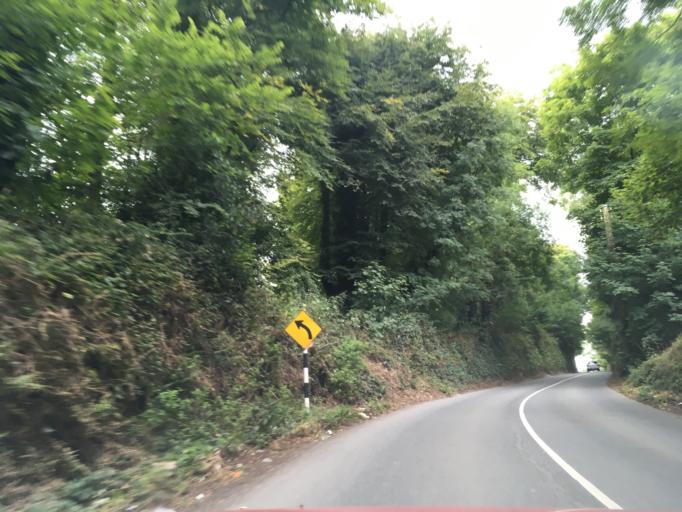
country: IE
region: Munster
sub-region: County Cork
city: Crosshaven
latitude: 51.7975
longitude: -8.2969
